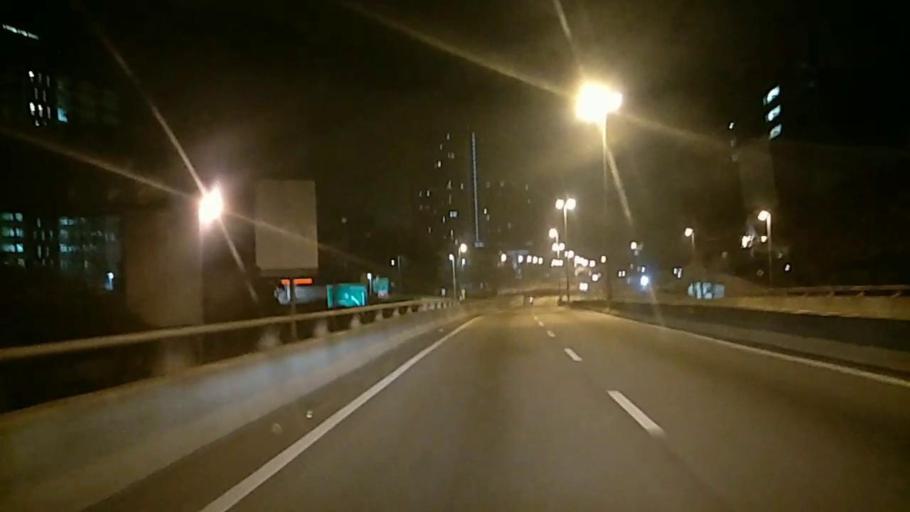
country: MY
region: Selangor
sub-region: Petaling
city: Petaling Jaya
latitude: 3.1068
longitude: 101.5963
